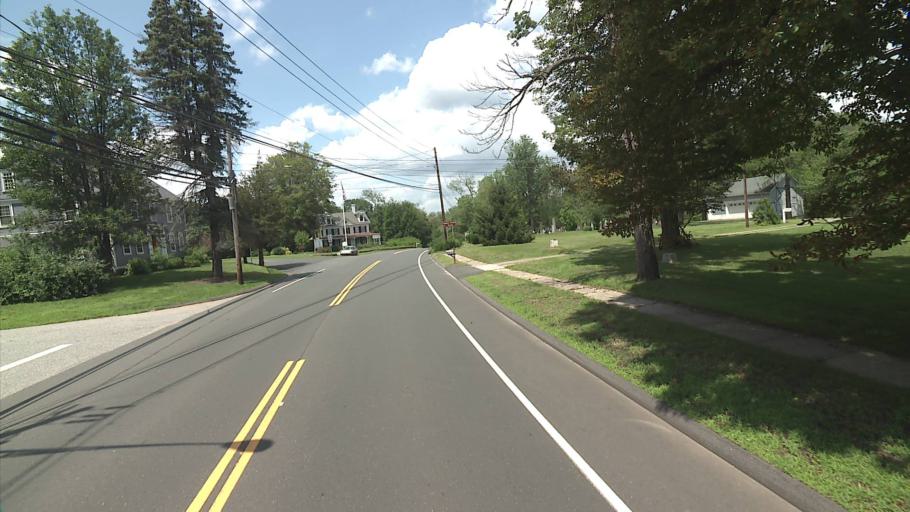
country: US
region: Connecticut
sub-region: Middlesex County
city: Higganum
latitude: 41.4803
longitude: -72.5158
